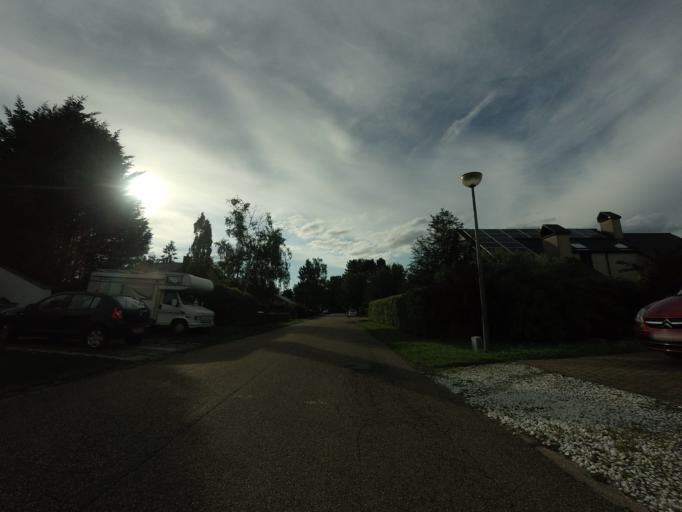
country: BE
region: Flanders
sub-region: Provincie Vlaams-Brabant
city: Boortmeerbeek
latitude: 50.9721
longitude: 4.5481
